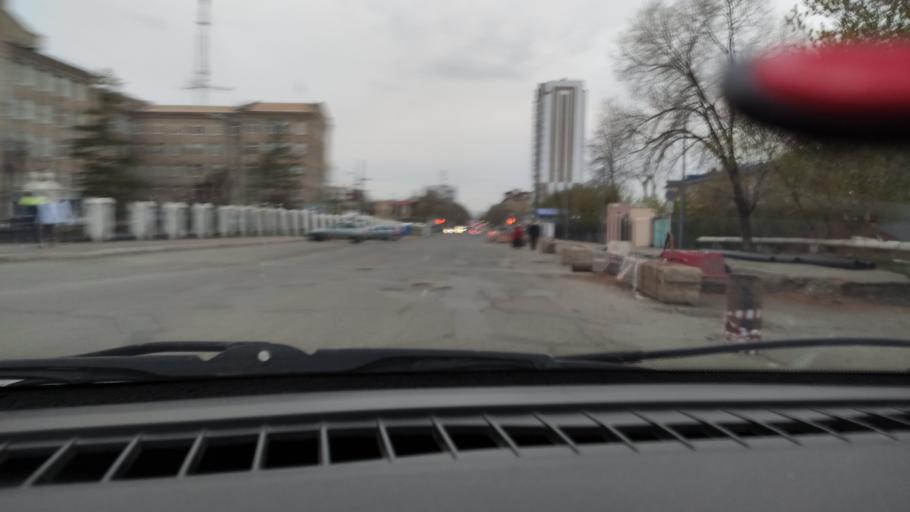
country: RU
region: Orenburg
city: Orenburg
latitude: 51.7751
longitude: 55.1213
